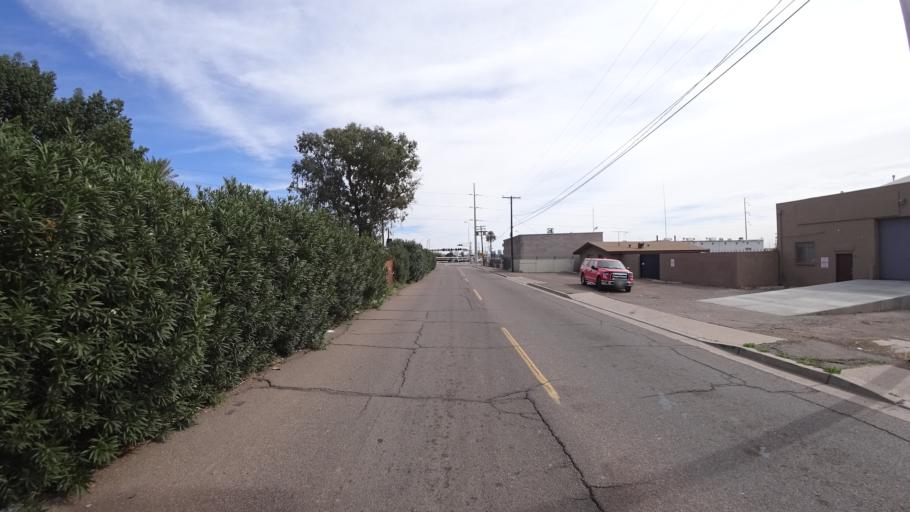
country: US
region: Arizona
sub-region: Maricopa County
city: Phoenix
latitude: 33.4876
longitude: -112.1274
